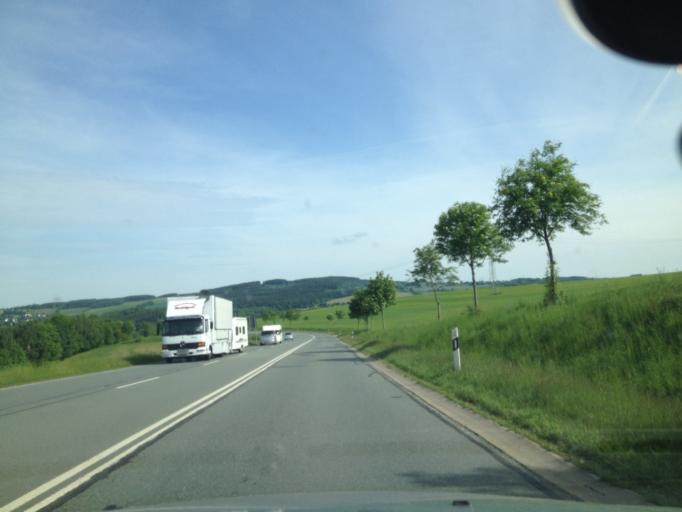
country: DE
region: Saxony
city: Annaberg-Buchholz
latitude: 50.5962
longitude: 13.0017
